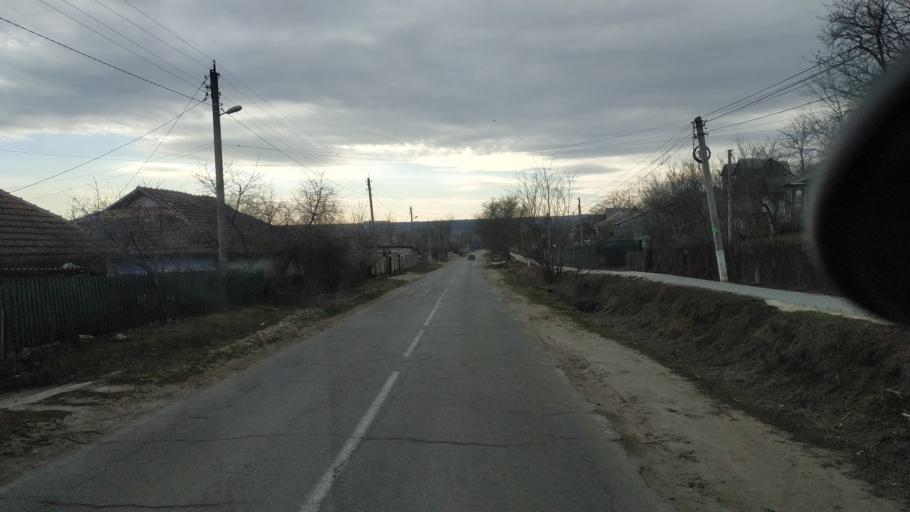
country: MD
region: Chisinau
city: Vadul lui Voda
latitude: 47.1475
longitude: 29.0788
